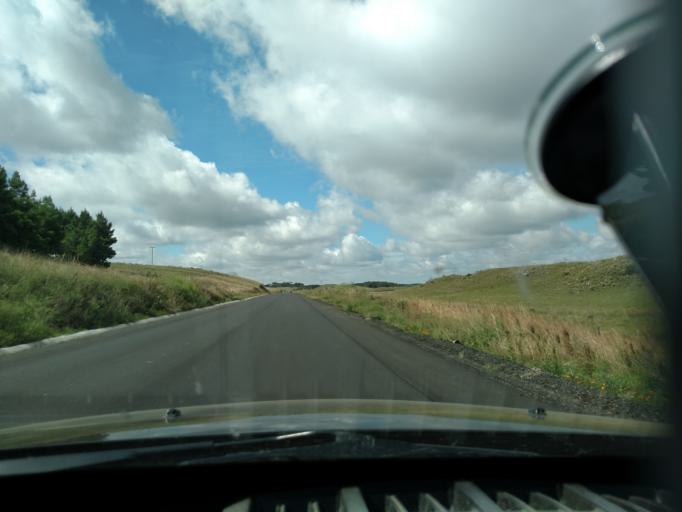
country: BR
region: Santa Catarina
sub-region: Lages
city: Lages
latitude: -28.0099
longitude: -50.0857
